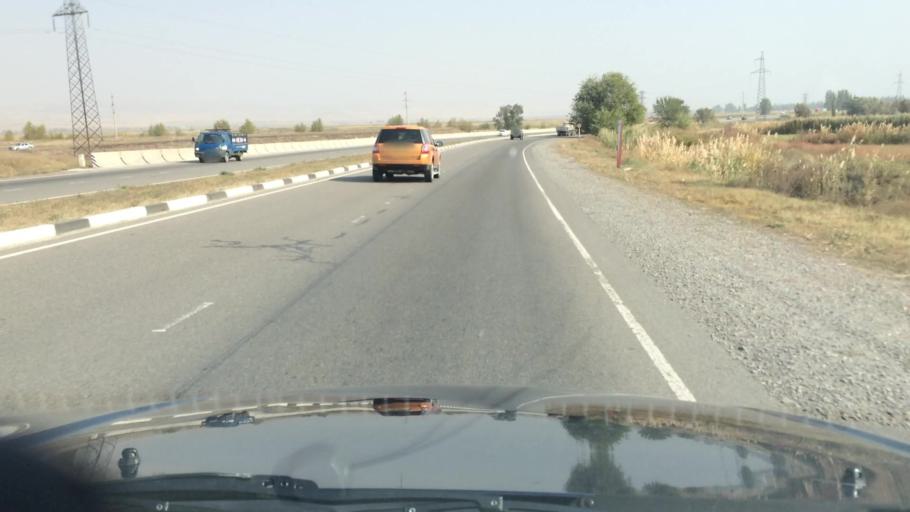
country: KG
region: Chuy
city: Kant
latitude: 42.9634
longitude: 74.8072
